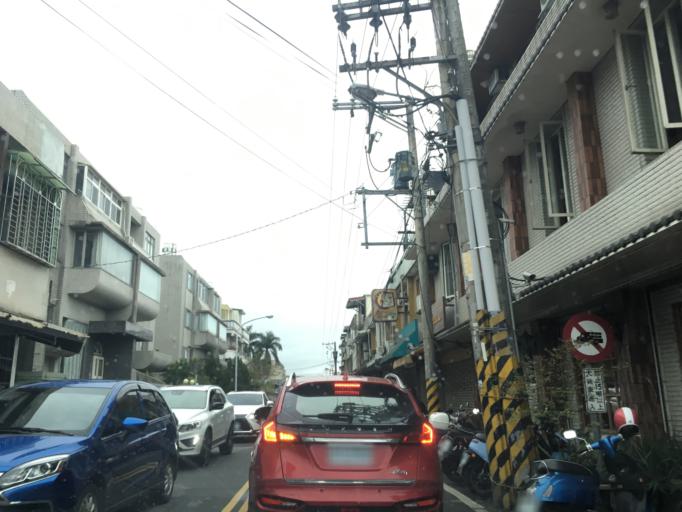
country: TW
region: Taiwan
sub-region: Hualien
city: Hualian
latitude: 23.9936
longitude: 121.5731
